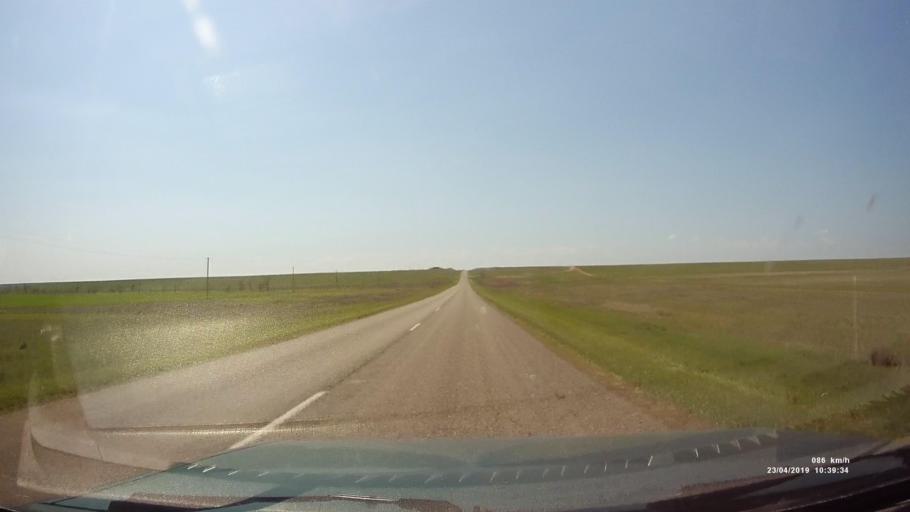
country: RU
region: Kalmykiya
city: Yashalta
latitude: 46.5175
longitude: 42.6387
